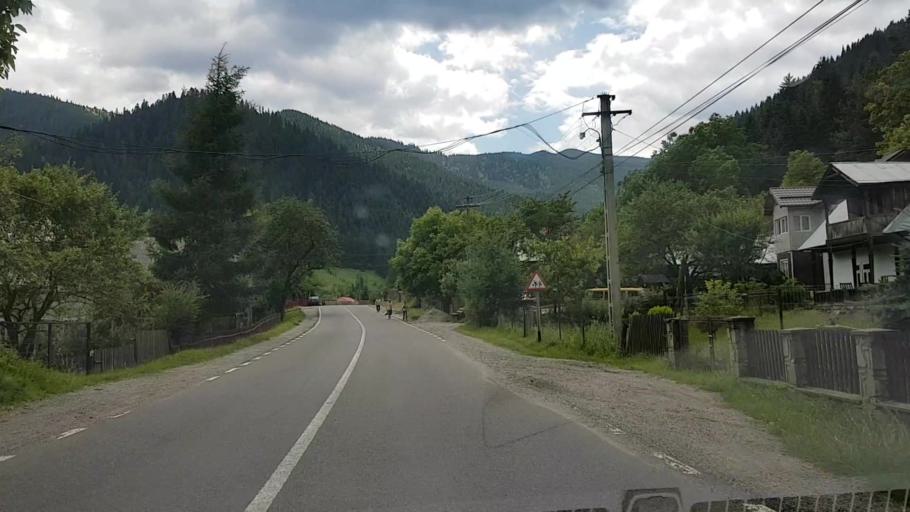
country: RO
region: Neamt
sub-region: Comuna Borca
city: Borca
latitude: 47.2066
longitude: 25.7523
